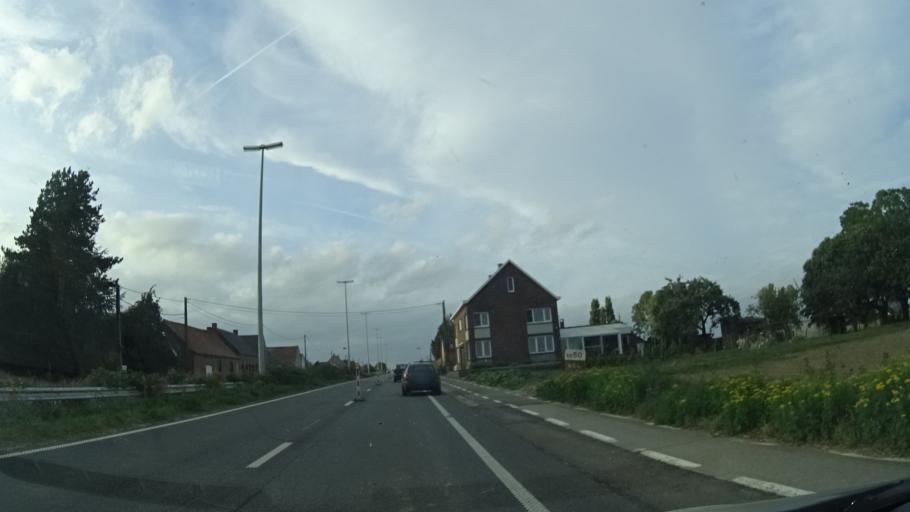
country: BE
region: Wallonia
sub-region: Province du Hainaut
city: Frasnes-lez-Buissenal
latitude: 50.6262
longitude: 3.6098
